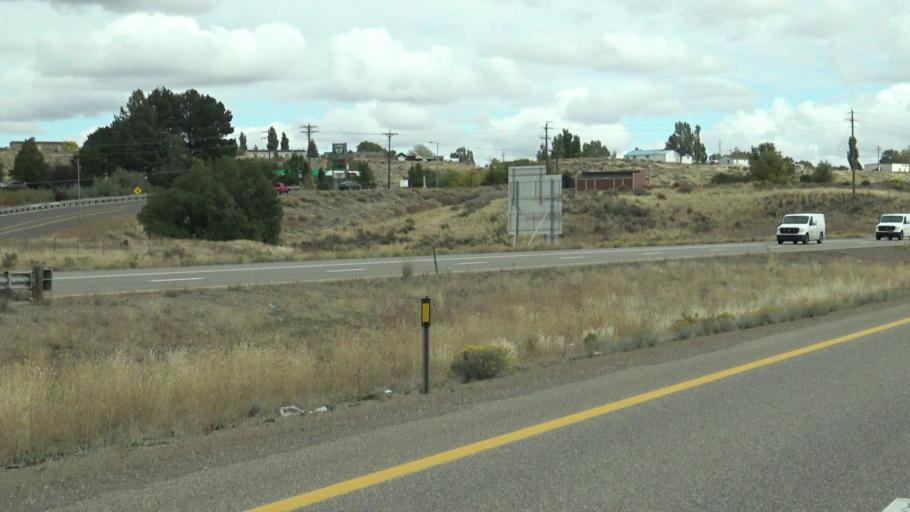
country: US
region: Nevada
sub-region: Elko County
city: Elko
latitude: 40.8448
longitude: -115.7690
